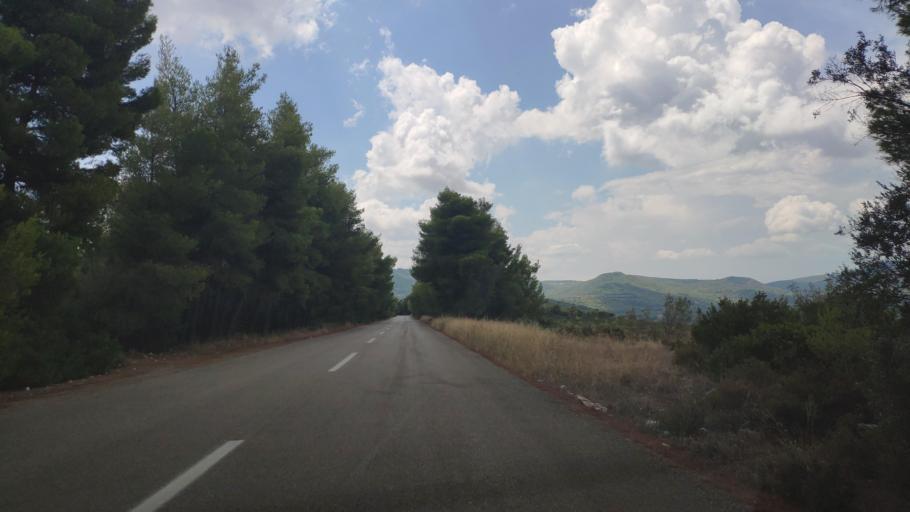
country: GR
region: Central Greece
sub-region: Nomos Fthiotidos
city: Malesina
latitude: 38.6360
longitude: 23.1756
